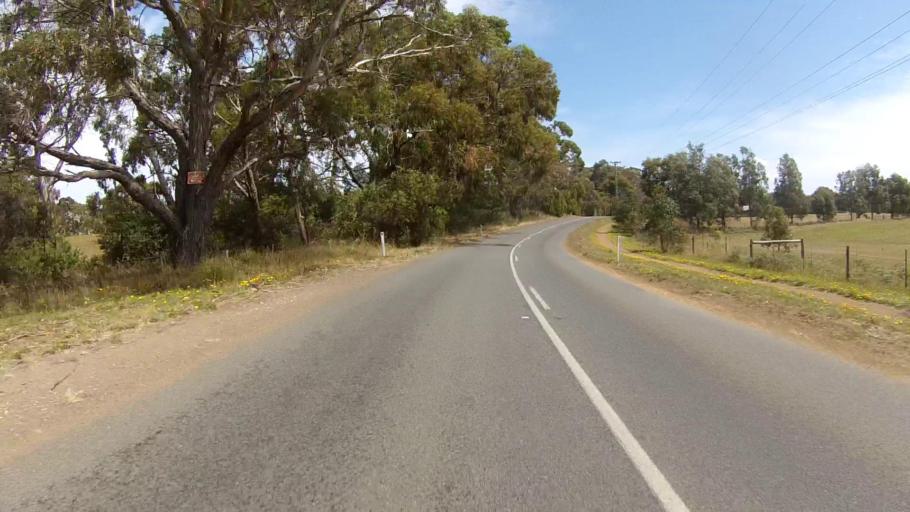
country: AU
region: Tasmania
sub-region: Kingborough
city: Blackmans Bay
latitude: -43.0294
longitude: 147.4280
